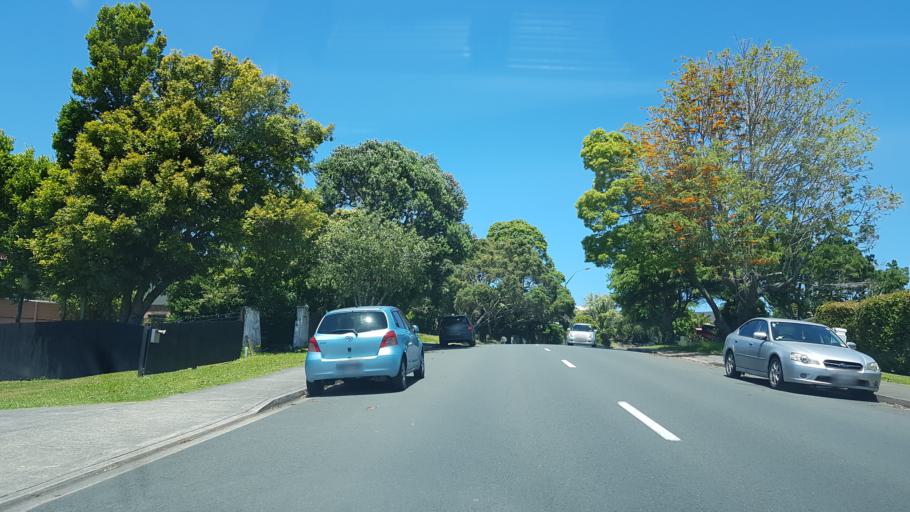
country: NZ
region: Auckland
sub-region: Auckland
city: North Shore
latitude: -36.7776
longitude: 174.7311
